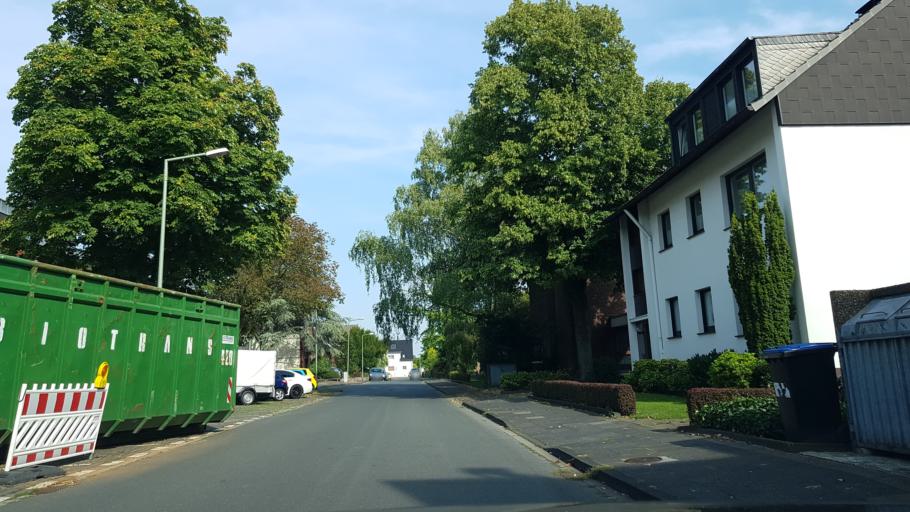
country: DE
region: North Rhine-Westphalia
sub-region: Regierungsbezirk Dusseldorf
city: Hochfeld
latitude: 51.3869
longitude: 6.7650
